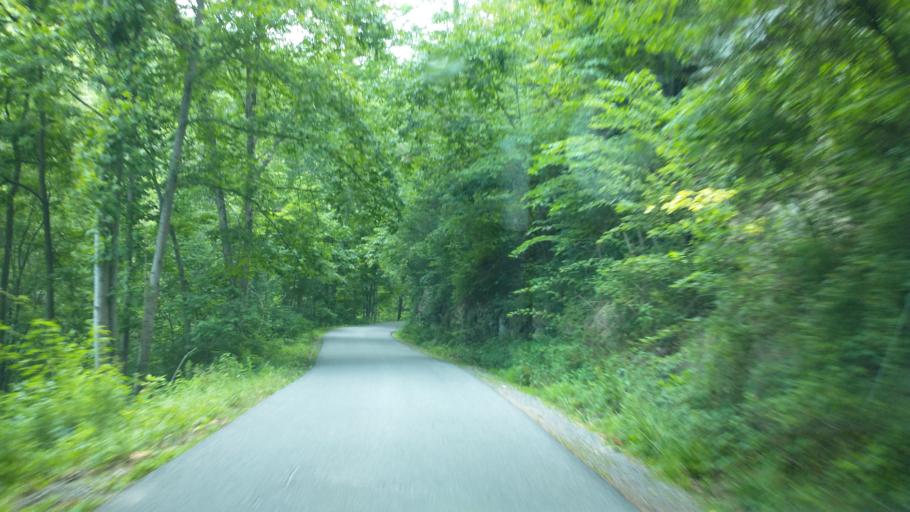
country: US
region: West Virginia
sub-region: Mercer County
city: Athens
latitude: 37.4658
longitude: -81.0619
